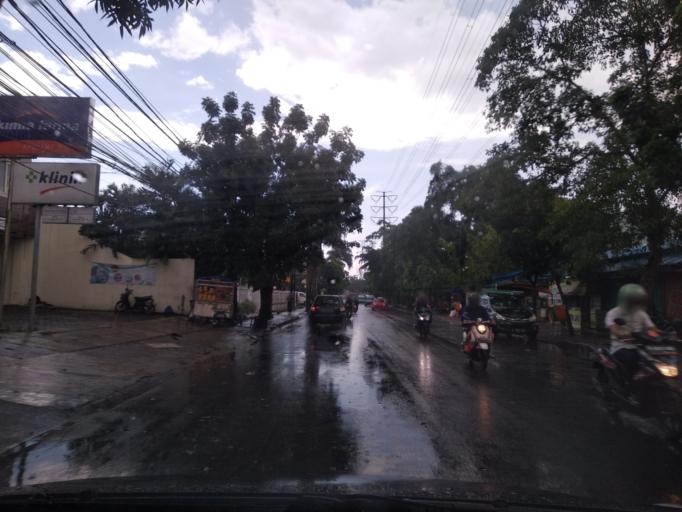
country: ID
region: Jakarta Raya
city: Jakarta
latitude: -6.2204
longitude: 106.8865
